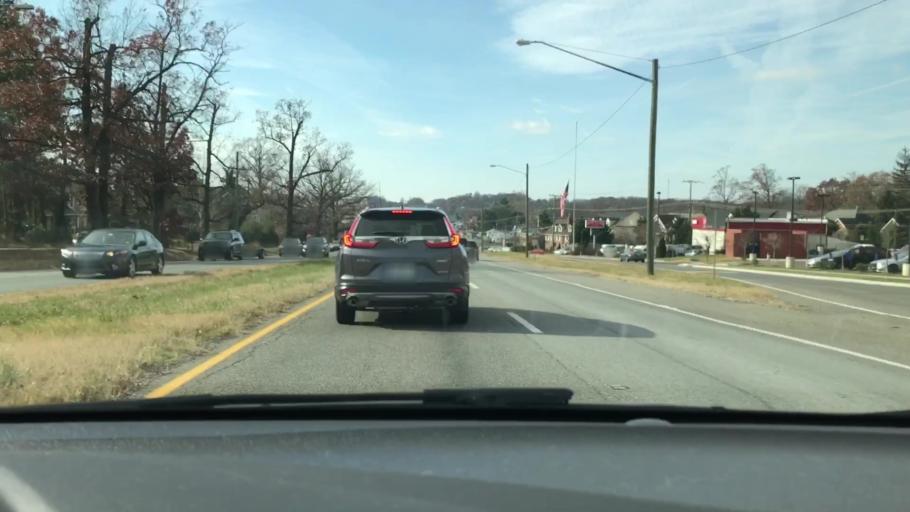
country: US
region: Virginia
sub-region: Fairfax County
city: Seven Corners
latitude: 38.8719
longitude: -77.1618
